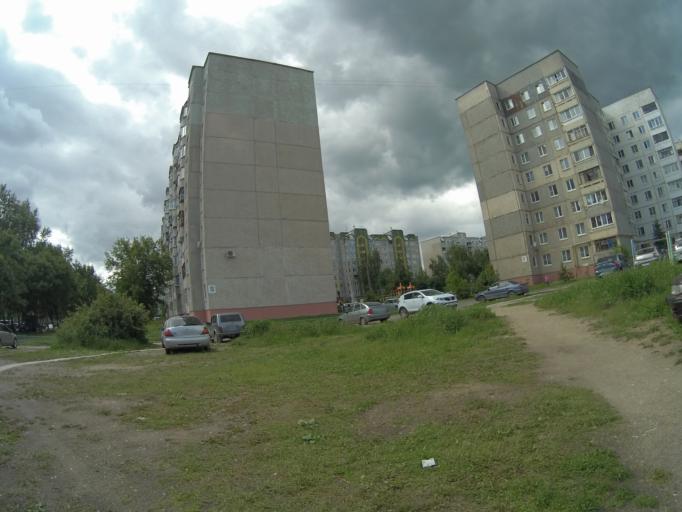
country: RU
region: Vladimir
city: Kommunar
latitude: 56.1679
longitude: 40.4484
